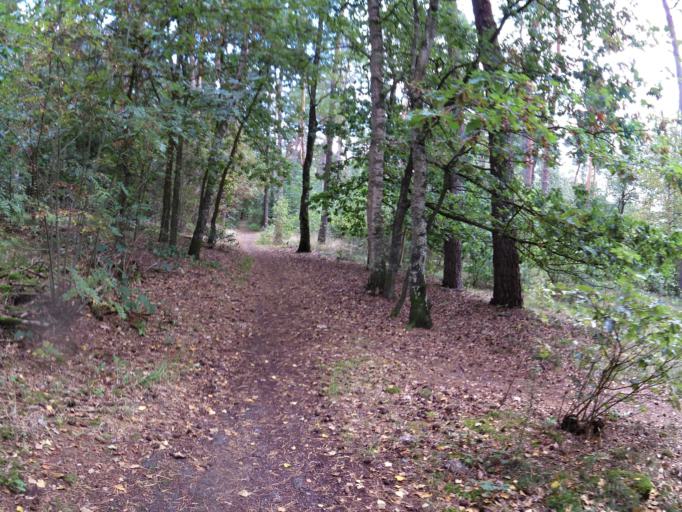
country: DE
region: Lower Saxony
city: Heeslingen
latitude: 53.3152
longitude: 9.3156
